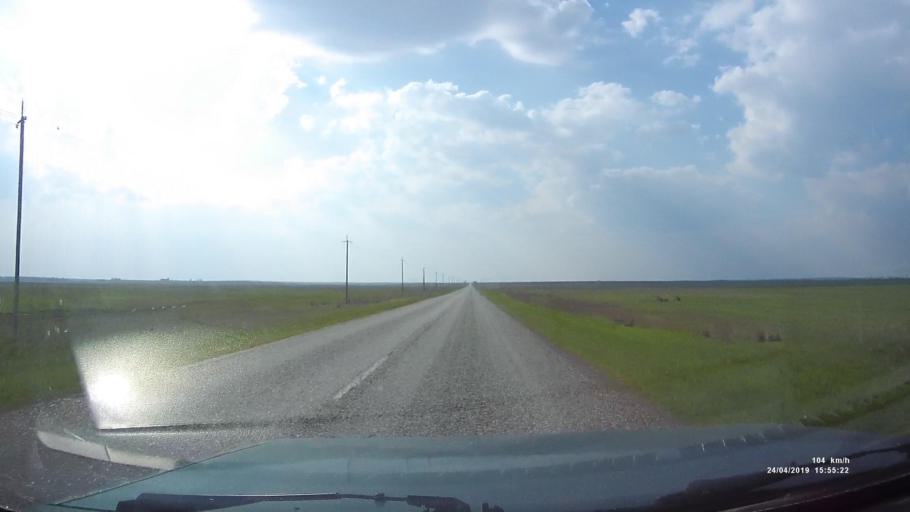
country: RU
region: Kalmykiya
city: Yashalta
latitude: 46.5899
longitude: 42.5508
